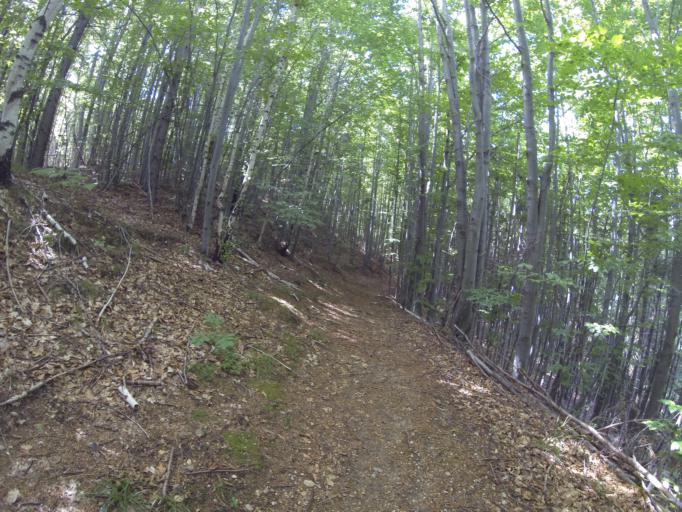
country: RO
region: Valcea
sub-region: Oras Baile Olanesti
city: Cheia
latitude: 45.2268
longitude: 24.1875
